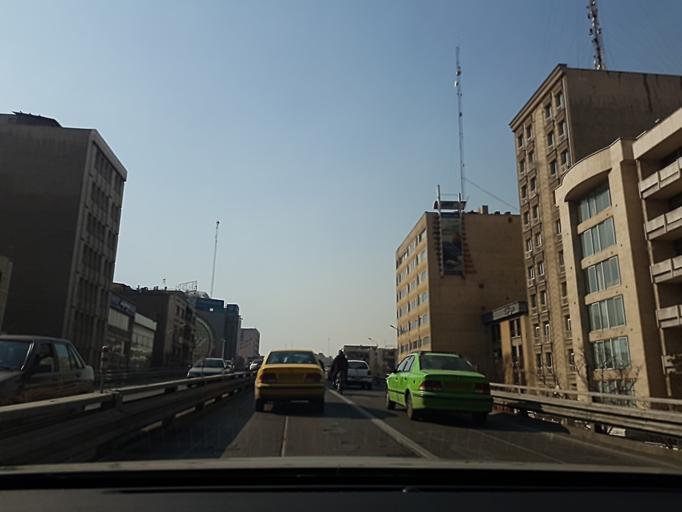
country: IR
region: Tehran
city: Tehran
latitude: 35.7153
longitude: 51.4191
